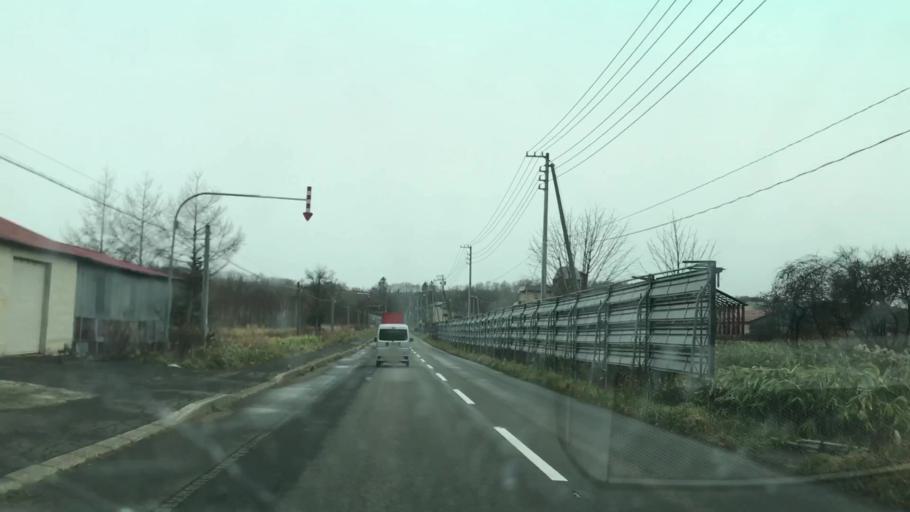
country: JP
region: Hokkaido
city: Yoichi
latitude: 43.3075
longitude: 140.5541
